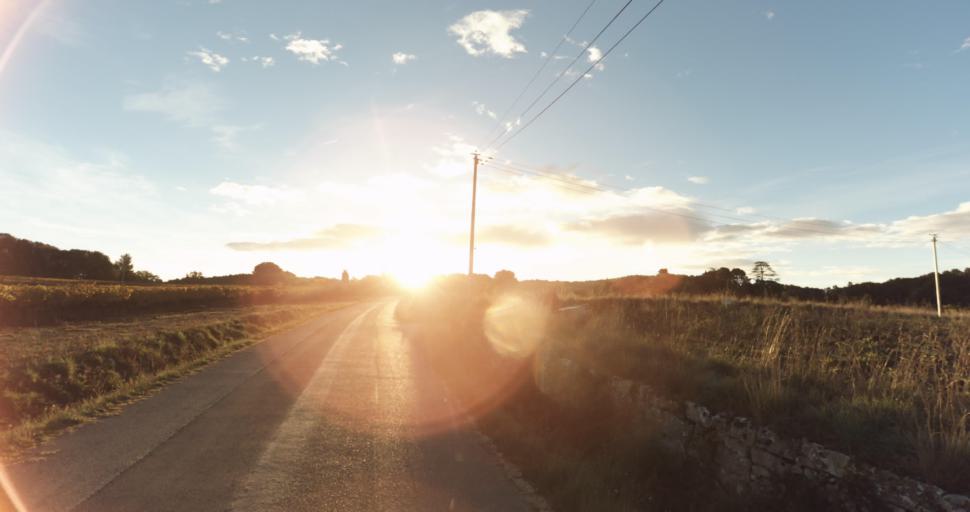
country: FR
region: Provence-Alpes-Cote d'Azur
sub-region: Departement des Bouches-du-Rhone
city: Venelles
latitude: 43.5780
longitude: 5.4798
